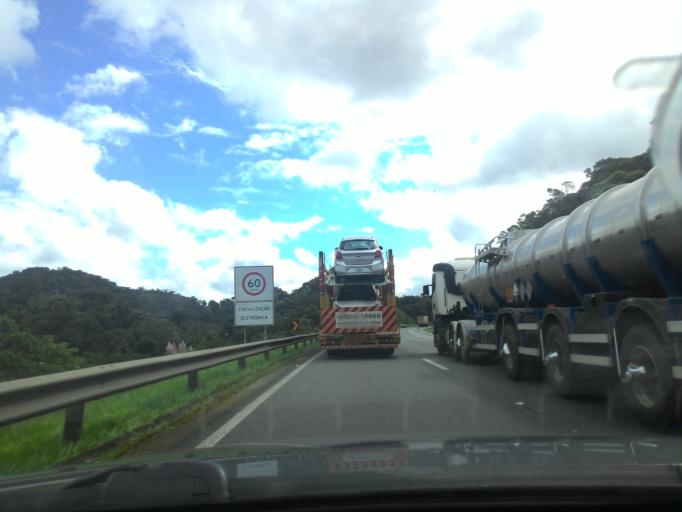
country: BR
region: Sao Paulo
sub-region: Cajati
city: Cajati
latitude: -24.9006
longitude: -48.2478
